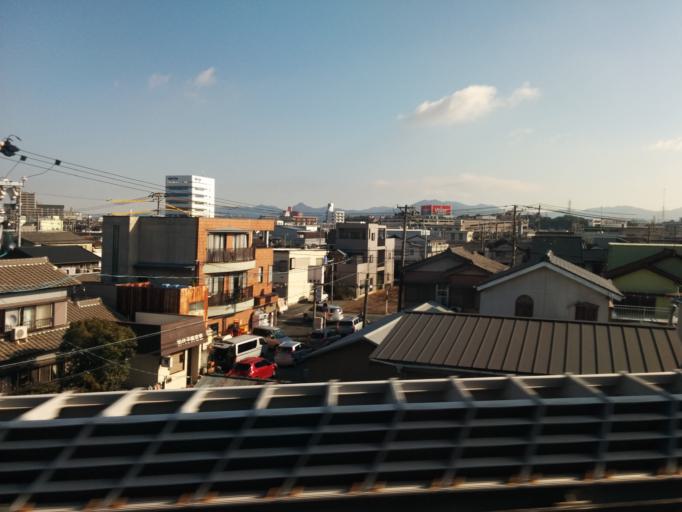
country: JP
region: Aichi
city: Toyohashi
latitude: 34.7523
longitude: 137.3874
